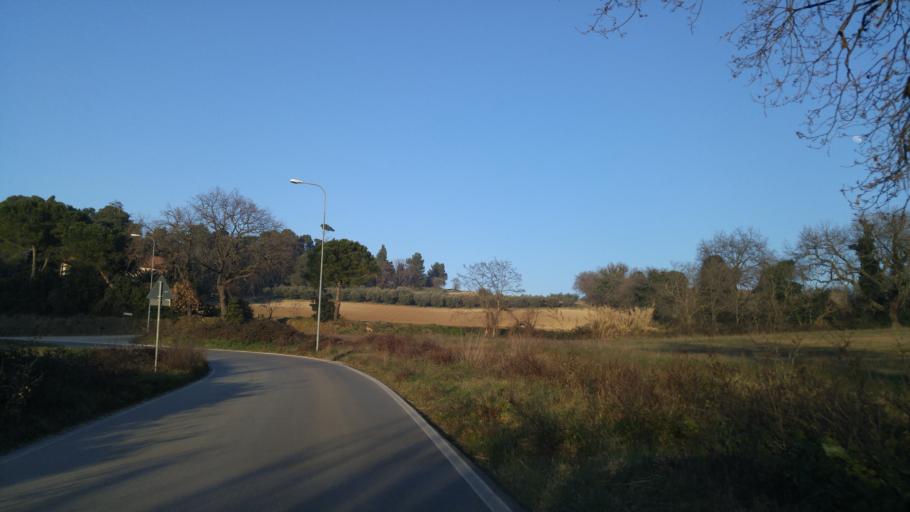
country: IT
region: The Marches
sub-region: Provincia di Pesaro e Urbino
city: Fenile
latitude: 43.8615
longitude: 12.9640
